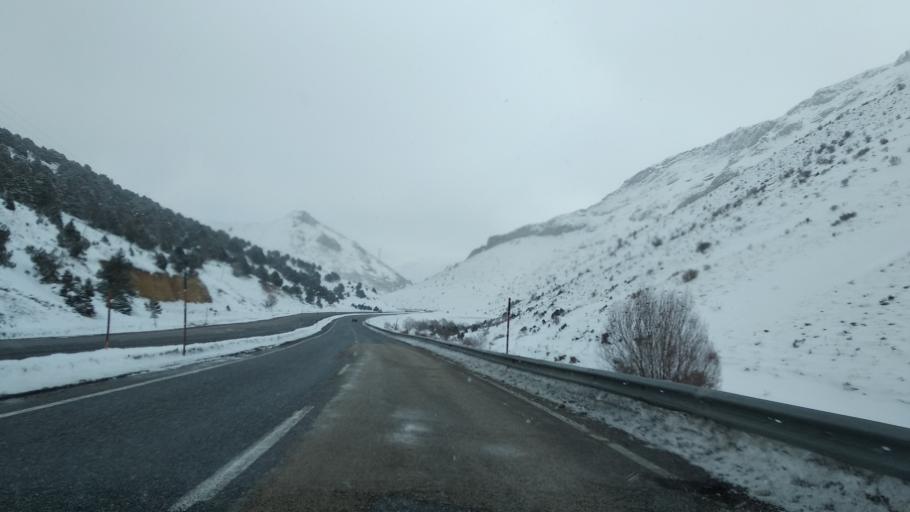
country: TR
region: Kayseri
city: Sariz
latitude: 38.5577
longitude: 36.4452
